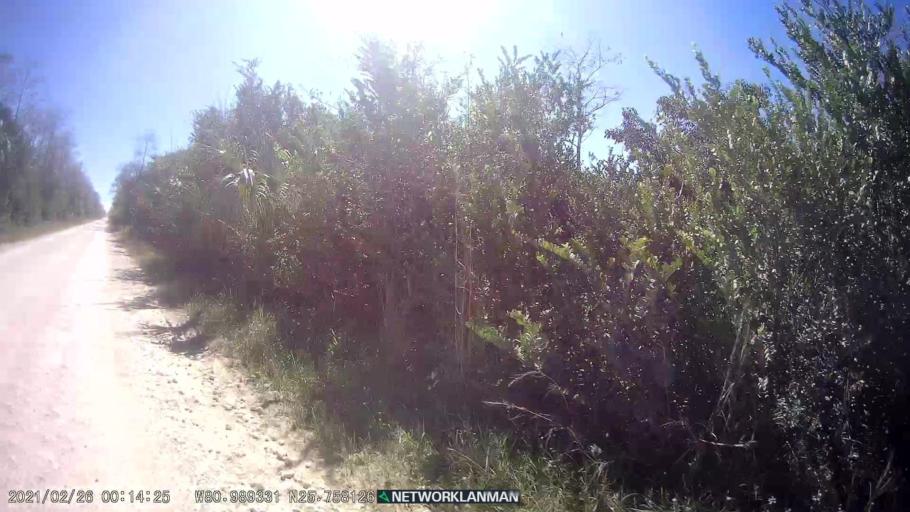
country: US
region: Florida
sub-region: Miami-Dade County
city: The Hammocks
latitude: 25.7579
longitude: -80.9887
